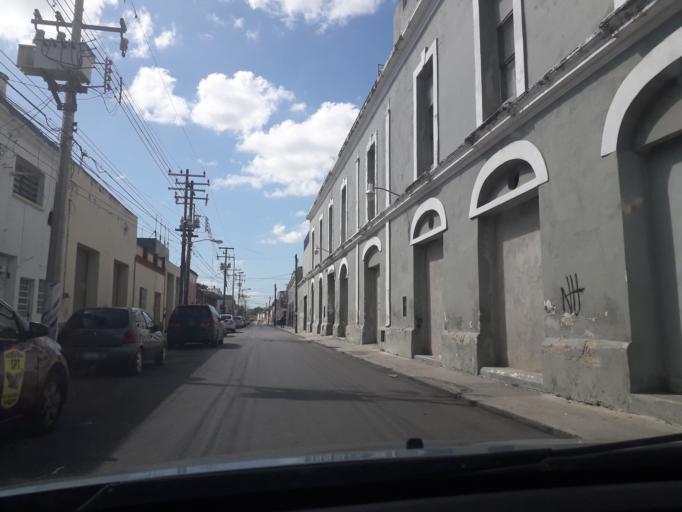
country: MX
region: Yucatan
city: Merida
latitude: 20.9596
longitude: -89.6235
